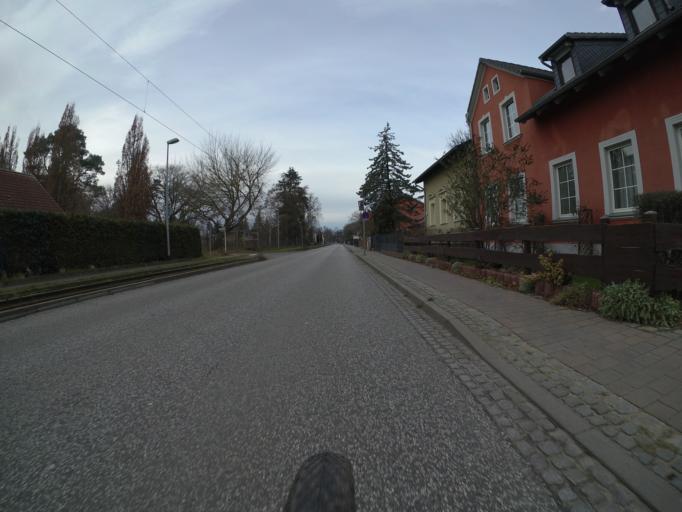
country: DE
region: Brandenburg
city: Schoneiche
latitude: 52.4782
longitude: 13.7061
